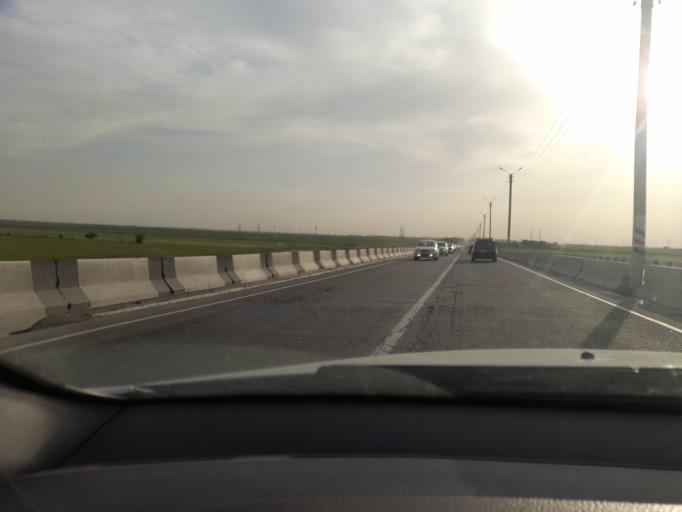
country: UZ
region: Navoiy
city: Beshrabot
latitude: 40.1326
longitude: 65.2219
